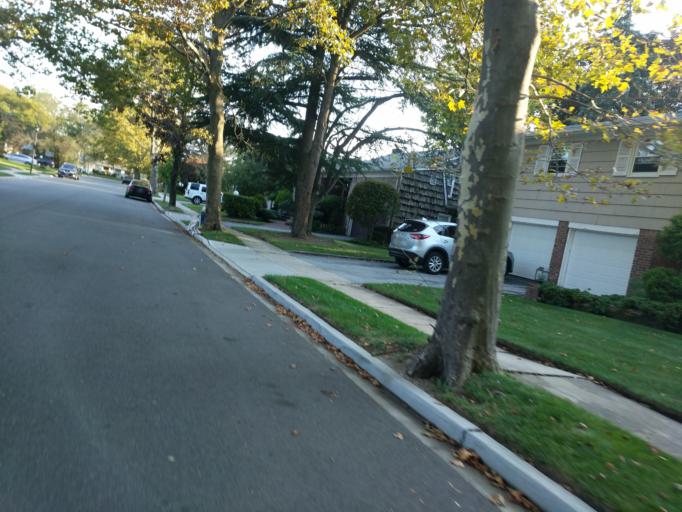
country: US
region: New York
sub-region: Nassau County
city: South Valley Stream
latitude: 40.6487
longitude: -73.7176
